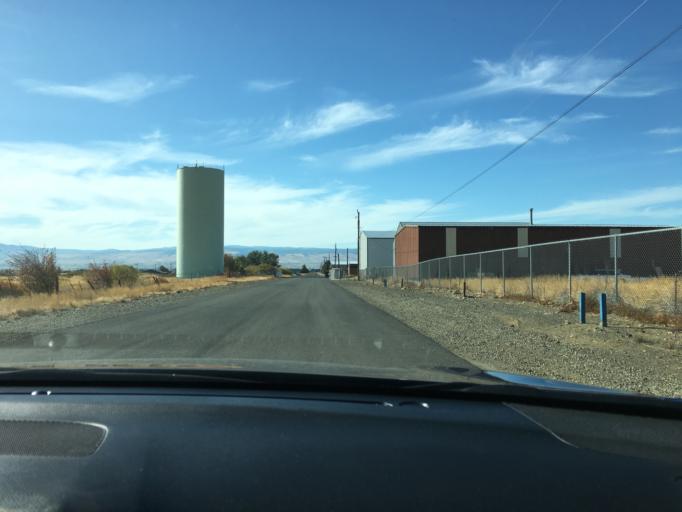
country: US
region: Washington
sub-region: Kittitas County
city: Ellensburg
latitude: 47.0289
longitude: -120.5264
